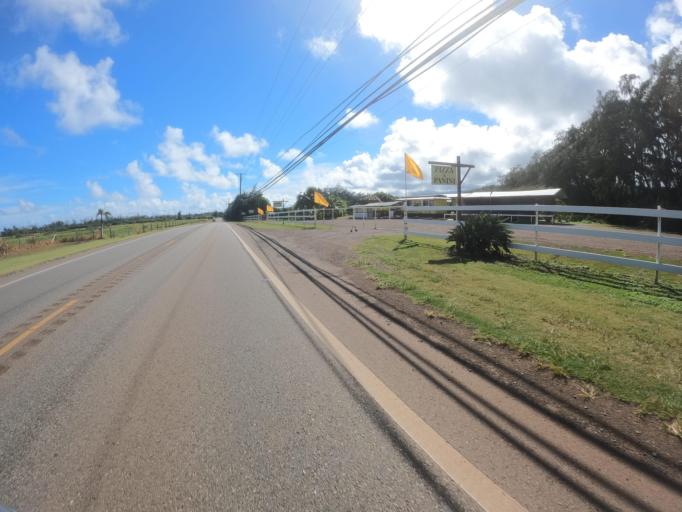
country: US
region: Hawaii
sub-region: Honolulu County
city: Kahuku
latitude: 21.6838
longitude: -157.9599
